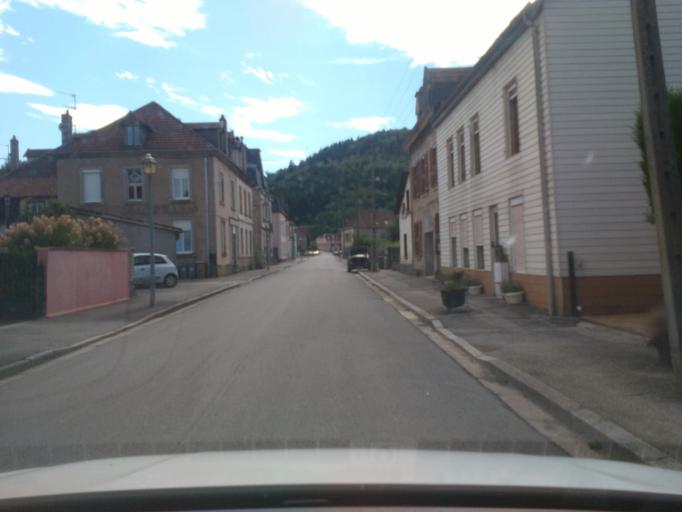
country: FR
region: Lorraine
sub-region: Departement des Vosges
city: Senones
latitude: 48.3925
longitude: 6.9765
